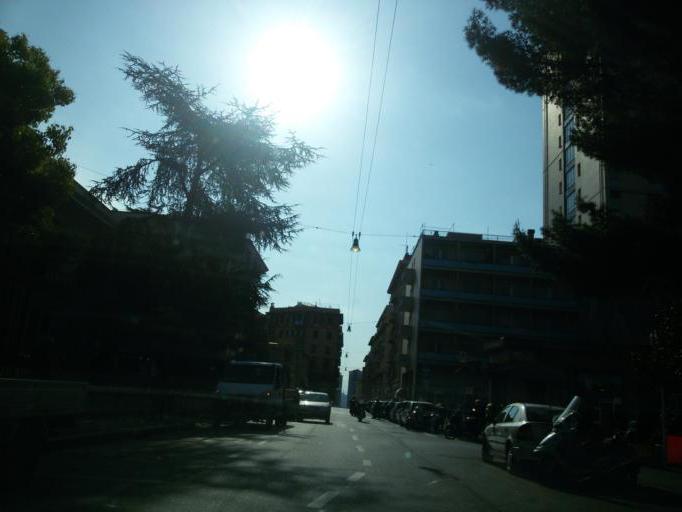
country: IT
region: Liguria
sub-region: Provincia di Genova
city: San Teodoro
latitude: 44.4125
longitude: 8.8969
